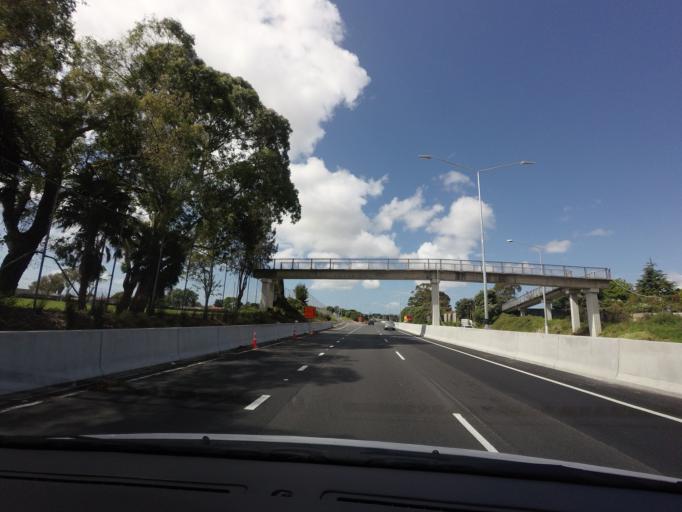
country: NZ
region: Auckland
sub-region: Auckland
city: Mangere
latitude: -36.9682
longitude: 174.7937
